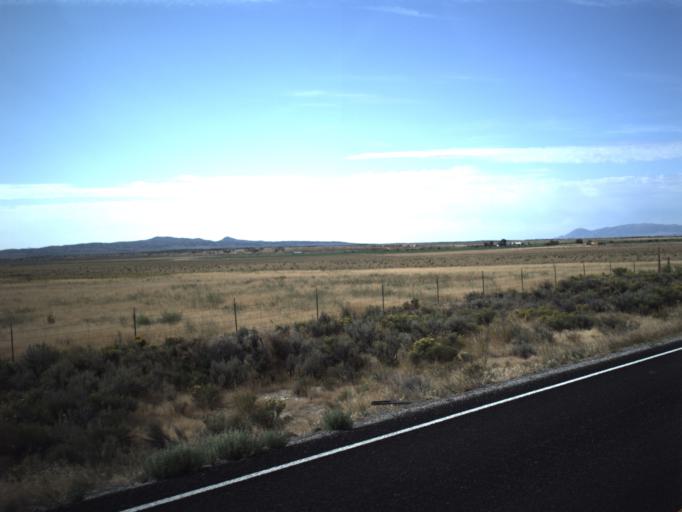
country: US
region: Idaho
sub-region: Cassia County
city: Burley
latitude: 41.7819
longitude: -113.4850
